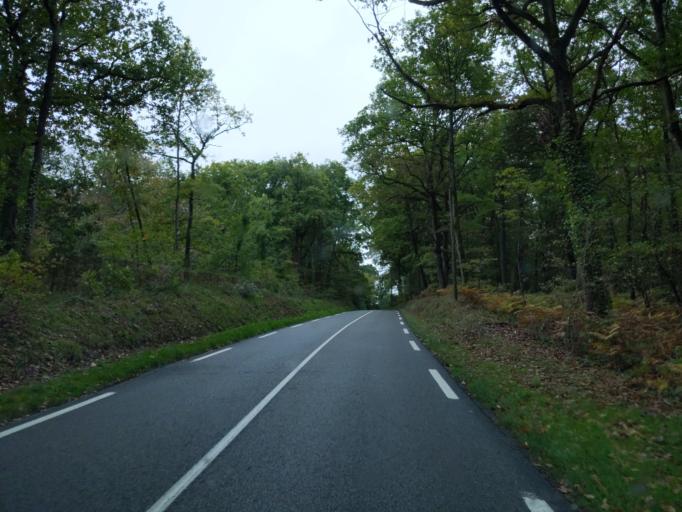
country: FR
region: Ile-de-France
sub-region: Departement des Yvelines
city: Saint-Arnoult-en-Yvelines
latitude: 48.5880
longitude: 1.9342
